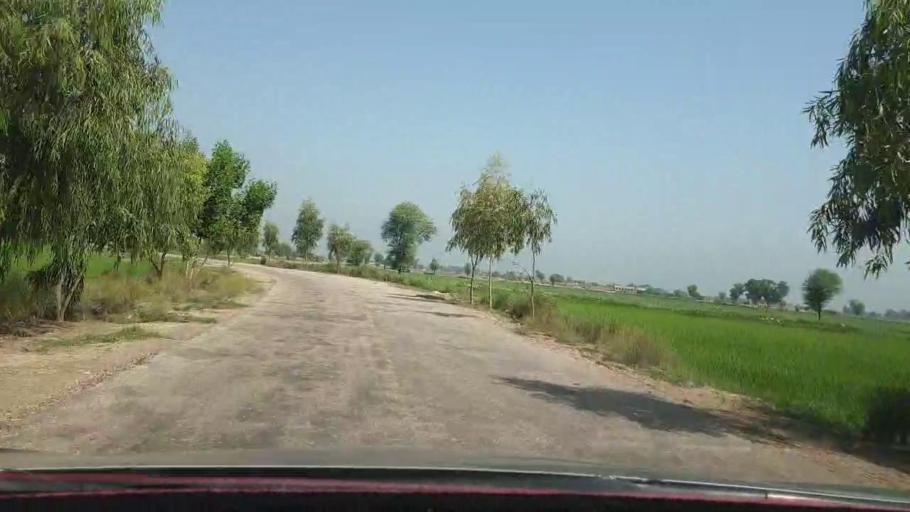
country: PK
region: Sindh
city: Warah
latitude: 27.4709
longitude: 67.8330
